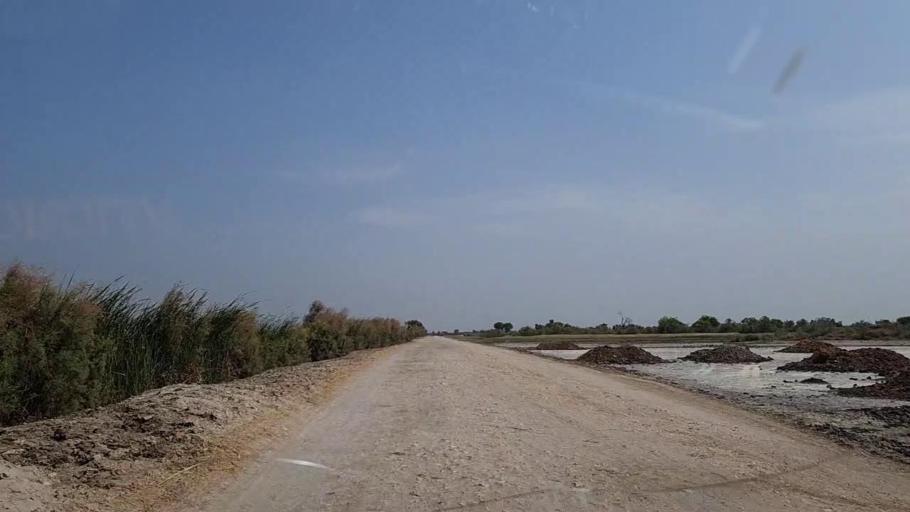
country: PK
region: Sindh
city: Khanpur
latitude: 27.8074
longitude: 69.3099
